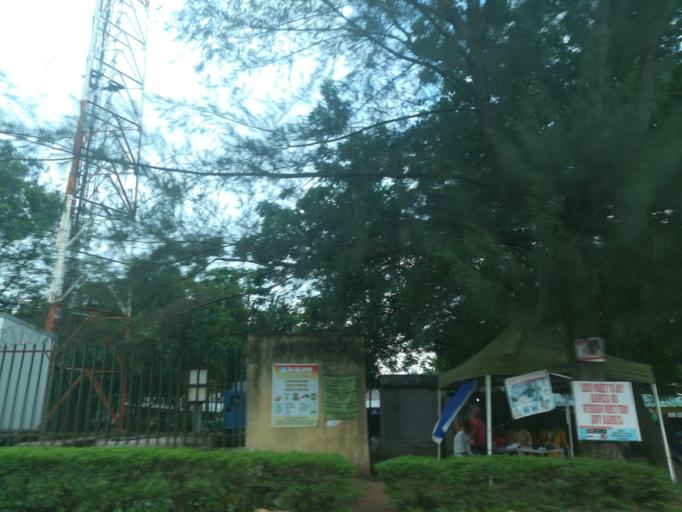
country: NG
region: Lagos
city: Ikorodu
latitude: 6.6428
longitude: 3.5238
